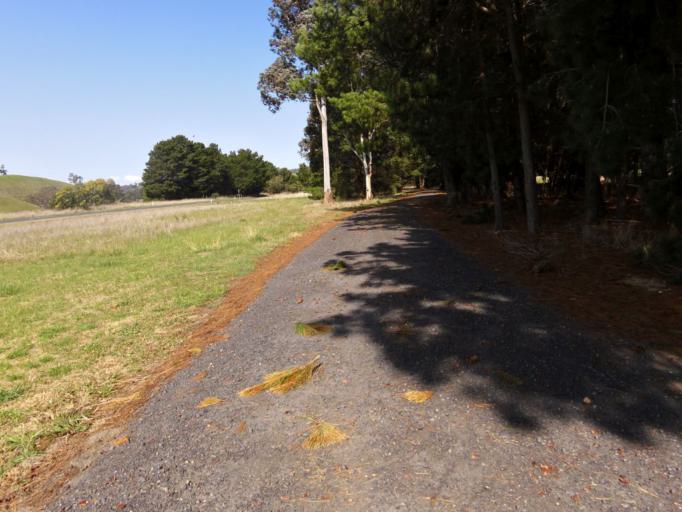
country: AU
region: Victoria
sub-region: Murrindindi
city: Alexandra
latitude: -37.0081
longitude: 145.7518
